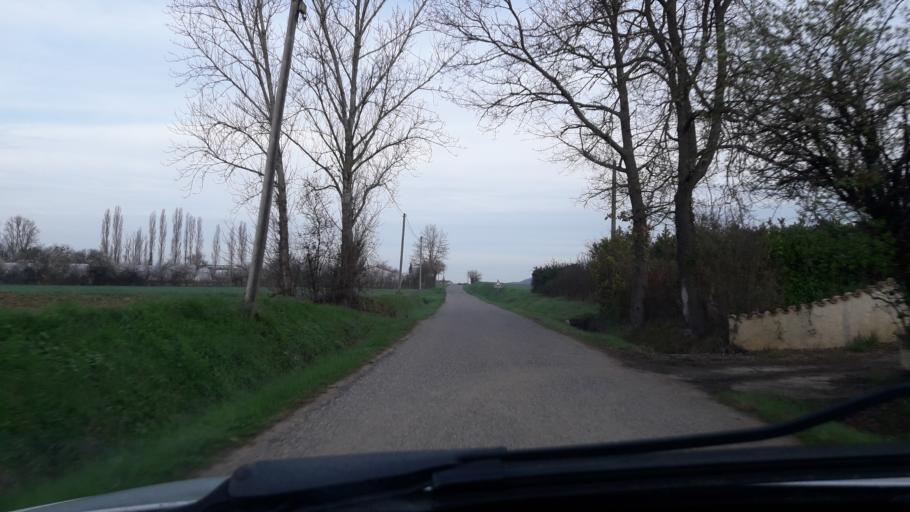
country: FR
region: Midi-Pyrenees
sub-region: Departement de la Haute-Garonne
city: Montesquieu-Volvestre
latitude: 43.1699
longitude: 1.2733
